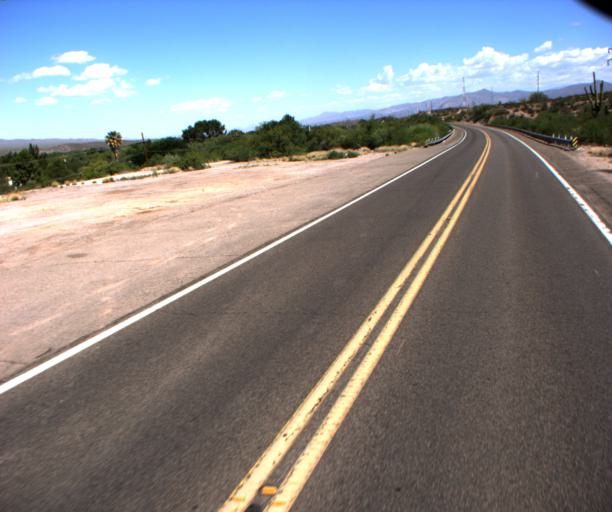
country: US
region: Arizona
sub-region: Pinal County
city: Mammoth
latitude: 32.9121
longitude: -110.7190
